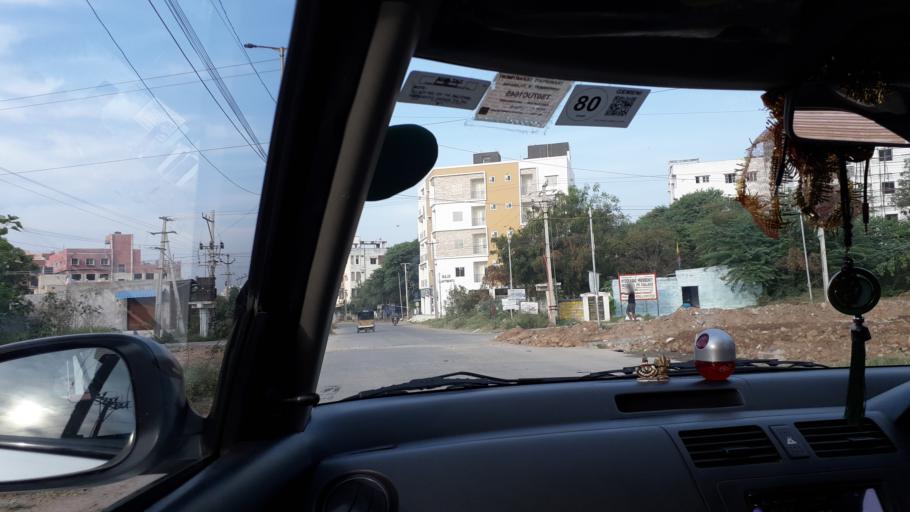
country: IN
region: Telangana
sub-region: Hyderabad
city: Hyderabad
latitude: 17.3948
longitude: 78.3828
